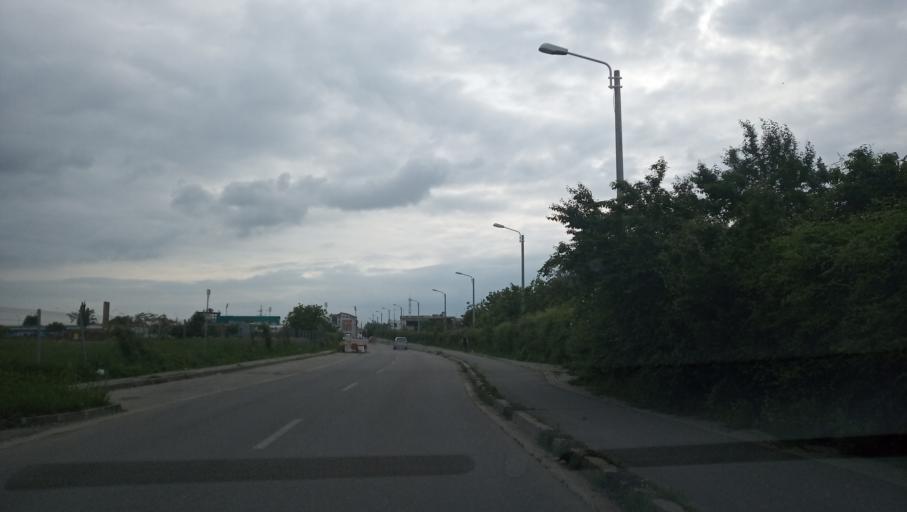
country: RO
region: Timis
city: Timisoara
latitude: 45.7471
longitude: 21.2582
